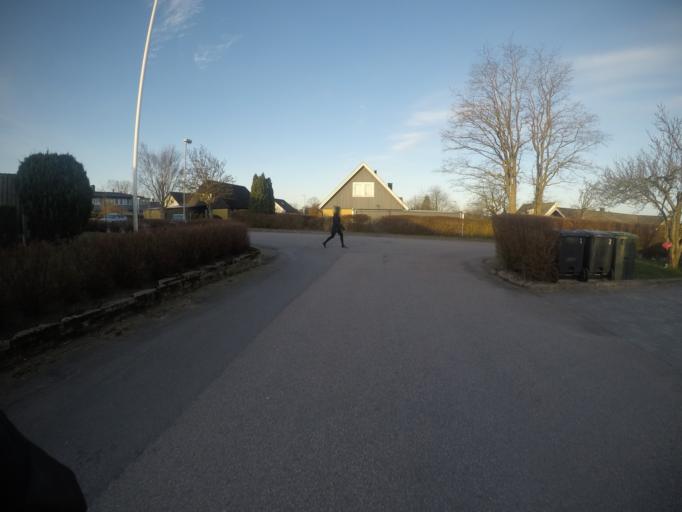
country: SE
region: Halland
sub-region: Laholms Kommun
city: Laholm
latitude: 56.5085
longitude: 13.0289
